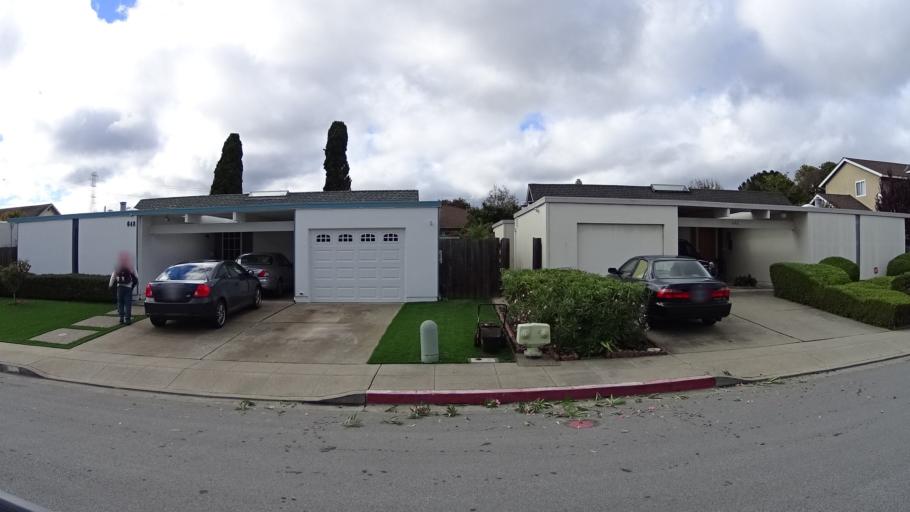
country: US
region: California
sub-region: San Mateo County
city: Foster City
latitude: 37.5625
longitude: -122.2660
